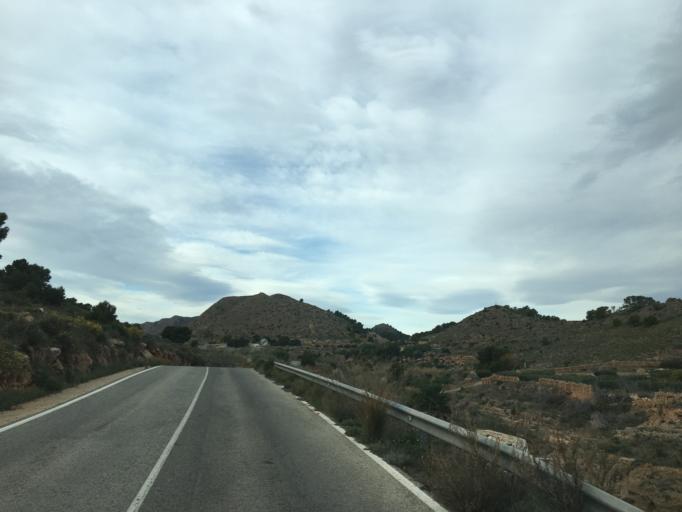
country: ES
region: Murcia
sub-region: Murcia
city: Fuente-Alamo de Murcia
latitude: 37.6124
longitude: -1.1056
